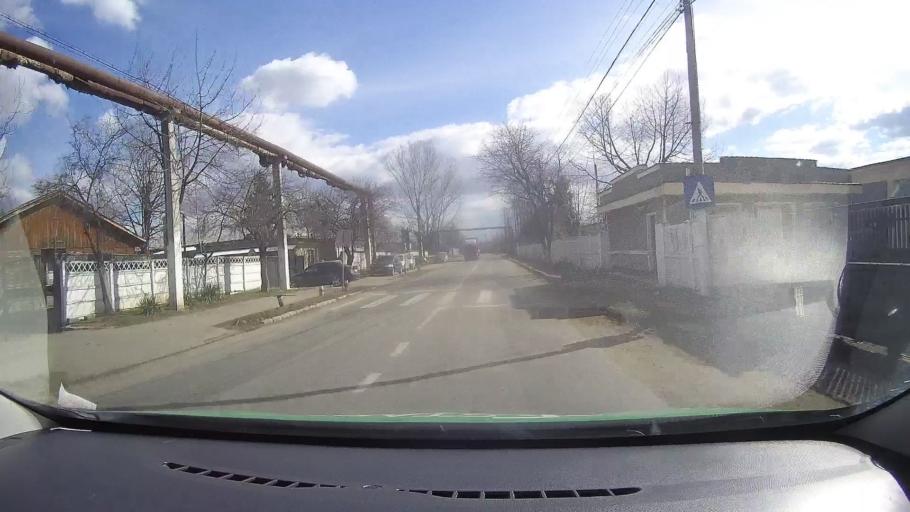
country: RO
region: Dambovita
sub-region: Municipiul Targoviste
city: Targoviste
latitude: 44.9421
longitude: 25.4392
